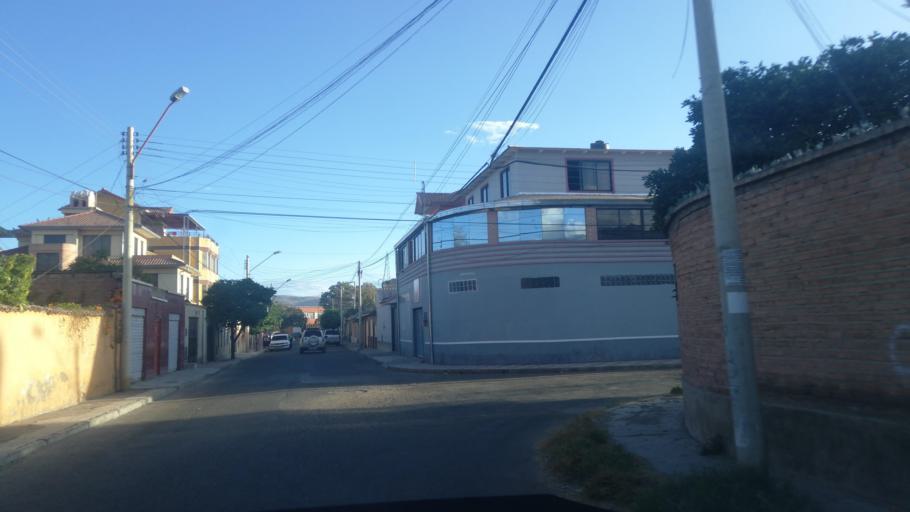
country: BO
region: Cochabamba
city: Cochabamba
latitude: -17.4091
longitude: -66.1710
